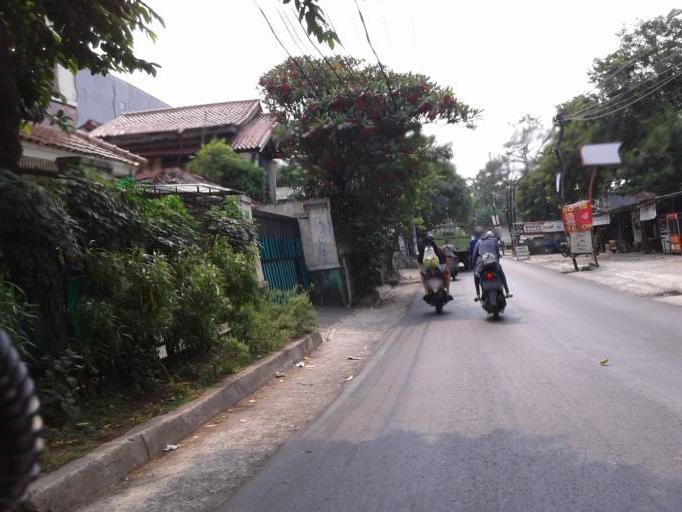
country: ID
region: Banten
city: South Tangerang
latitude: -6.2918
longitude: 106.7447
